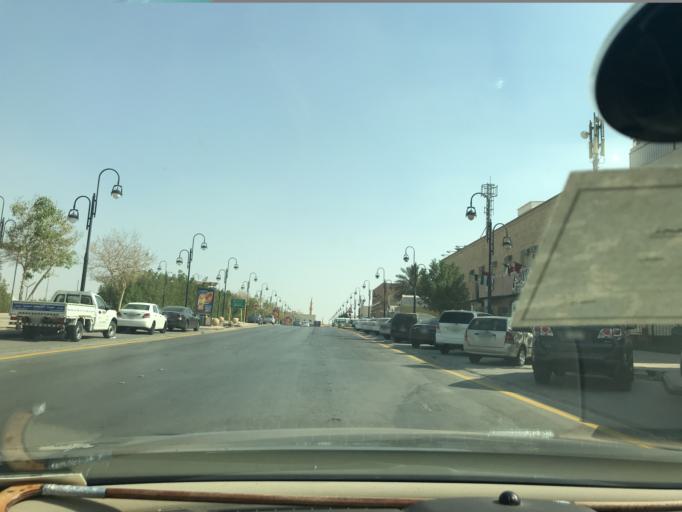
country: SA
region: Ar Riyad
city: Riyadh
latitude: 24.7428
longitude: 46.7658
